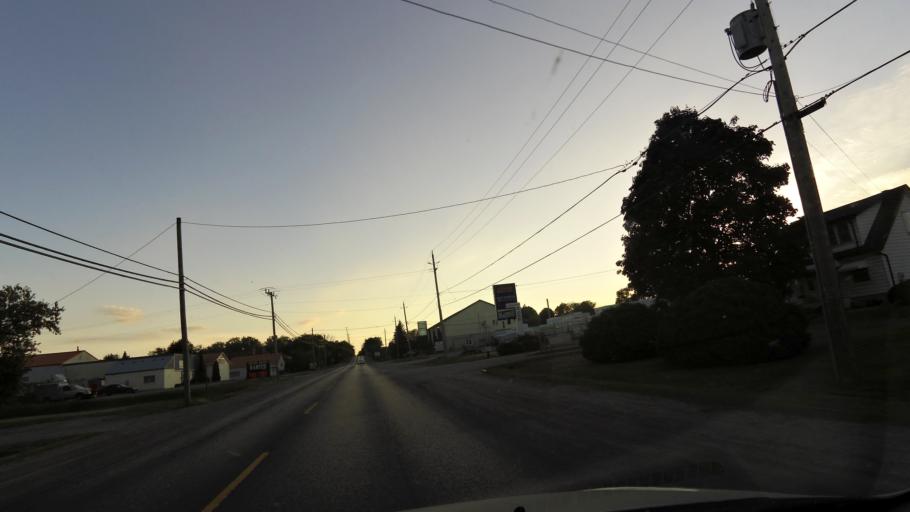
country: CA
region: Ontario
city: Peterborough
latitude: 44.3209
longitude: -78.2994
